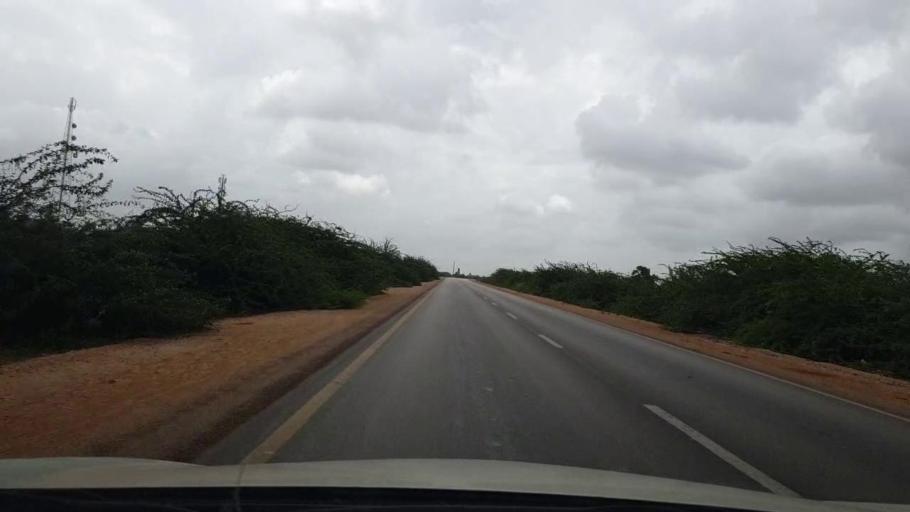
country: PK
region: Sindh
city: Mirpur Batoro
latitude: 24.6423
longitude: 68.4003
